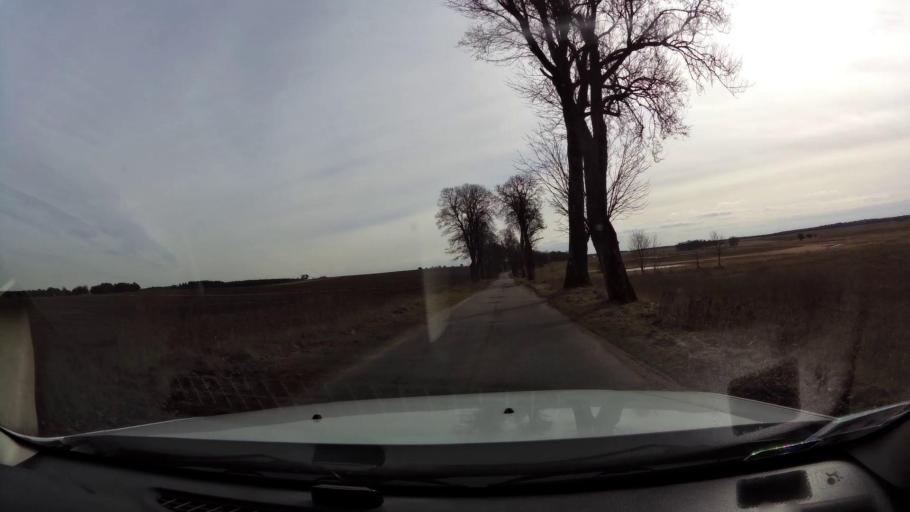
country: PL
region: West Pomeranian Voivodeship
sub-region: Powiat stargardzki
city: Insko
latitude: 53.4655
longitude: 15.6006
